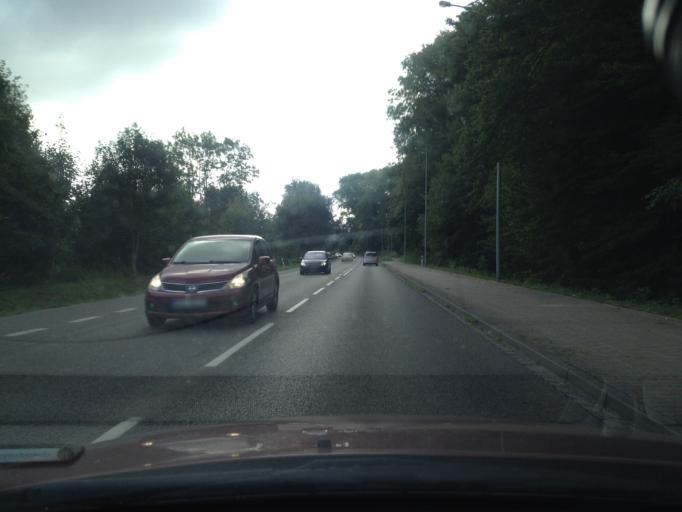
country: PL
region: West Pomeranian Voivodeship
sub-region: Powiat kamienski
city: Kamien Pomorski
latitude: 53.9659
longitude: 14.7834
